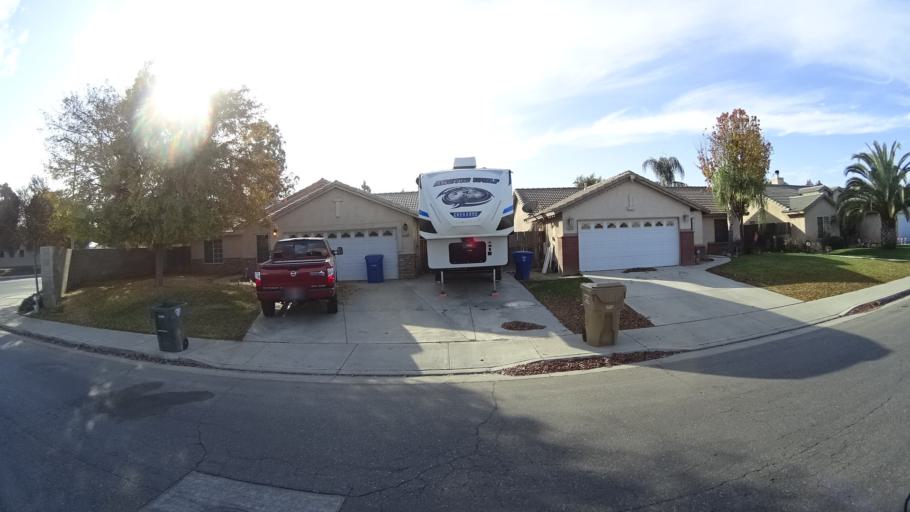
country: US
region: California
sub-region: Kern County
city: Rosedale
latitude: 35.4012
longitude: -119.1371
